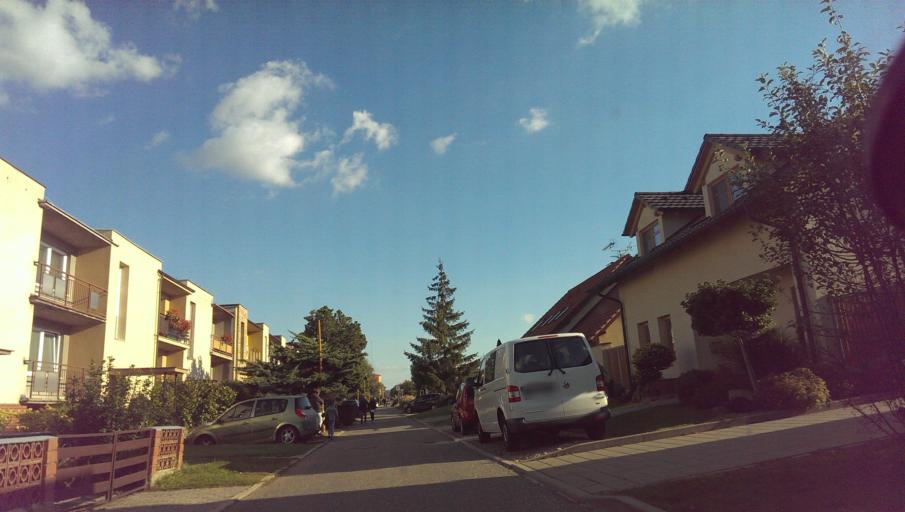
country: CZ
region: Zlin
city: Kunovice
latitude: 49.0612
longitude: 17.4776
